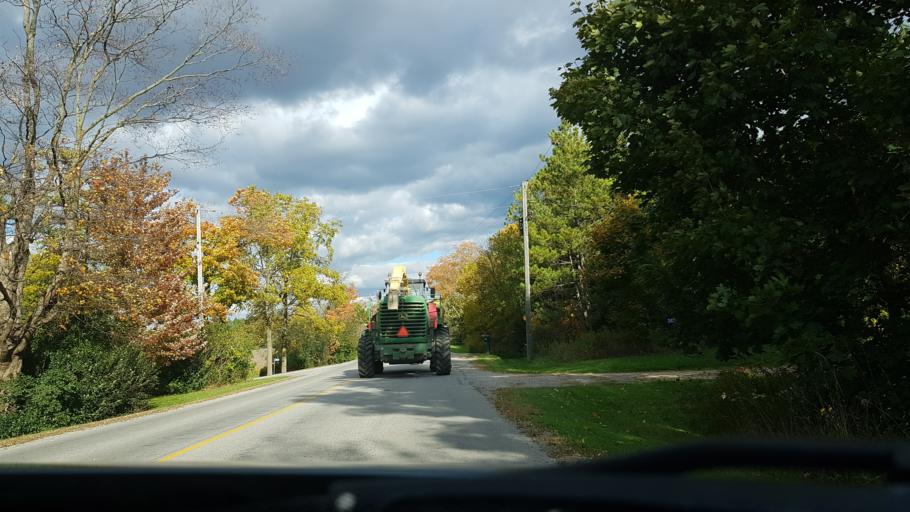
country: CA
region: Ontario
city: Delaware
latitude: 43.0130
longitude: -81.3751
